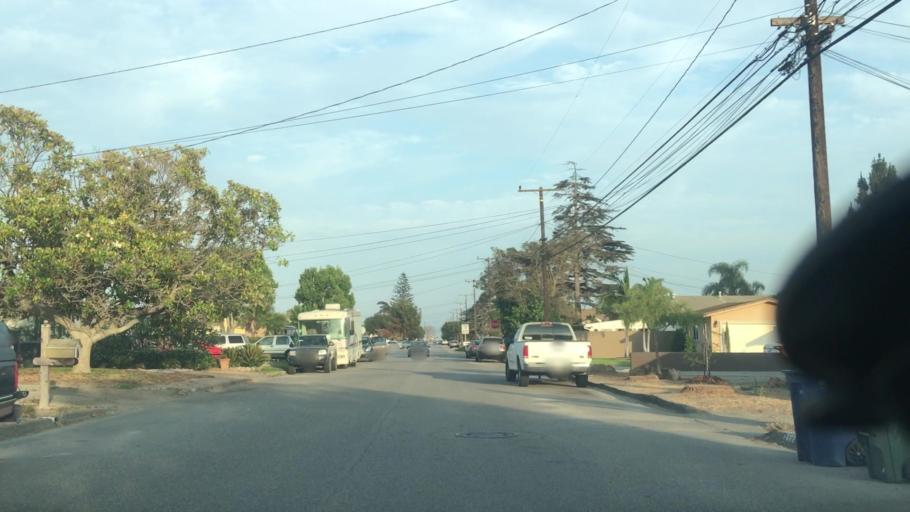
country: US
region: California
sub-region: Ventura County
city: El Rio
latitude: 34.2380
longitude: -119.1597
